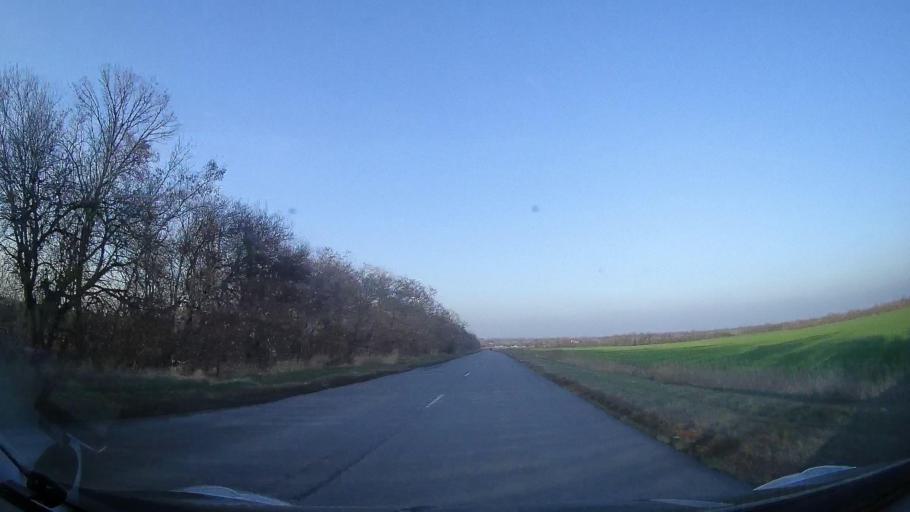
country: RU
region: Rostov
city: Kirovskaya
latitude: 47.0202
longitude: 39.9788
